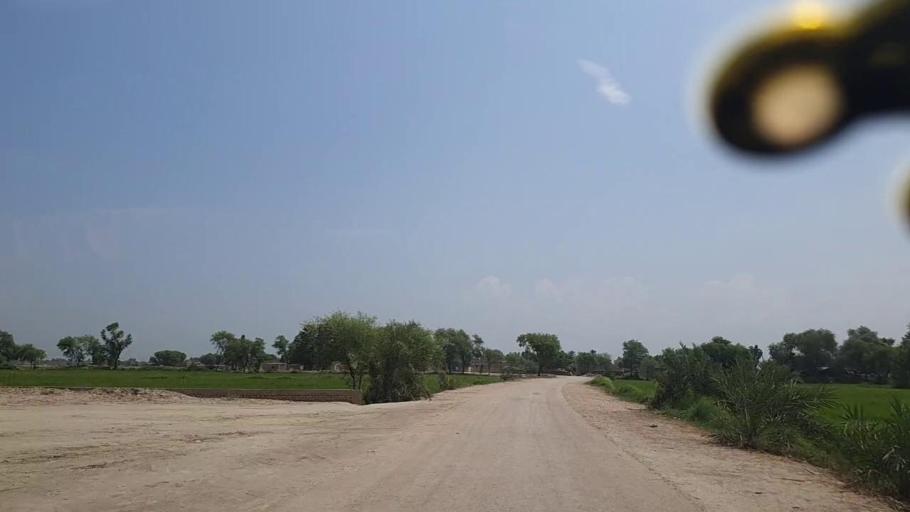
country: PK
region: Sindh
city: Rustam jo Goth
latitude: 28.1110
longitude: 68.8623
